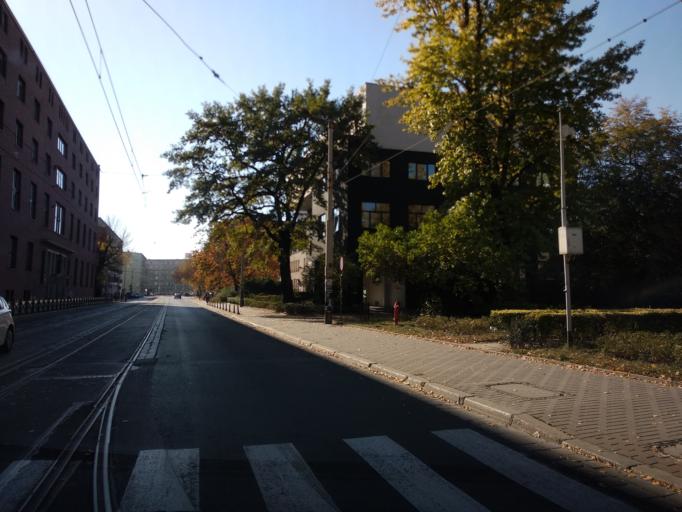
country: PL
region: Lower Silesian Voivodeship
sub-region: Powiat wroclawski
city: Wroclaw
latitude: 51.1066
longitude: 17.0245
